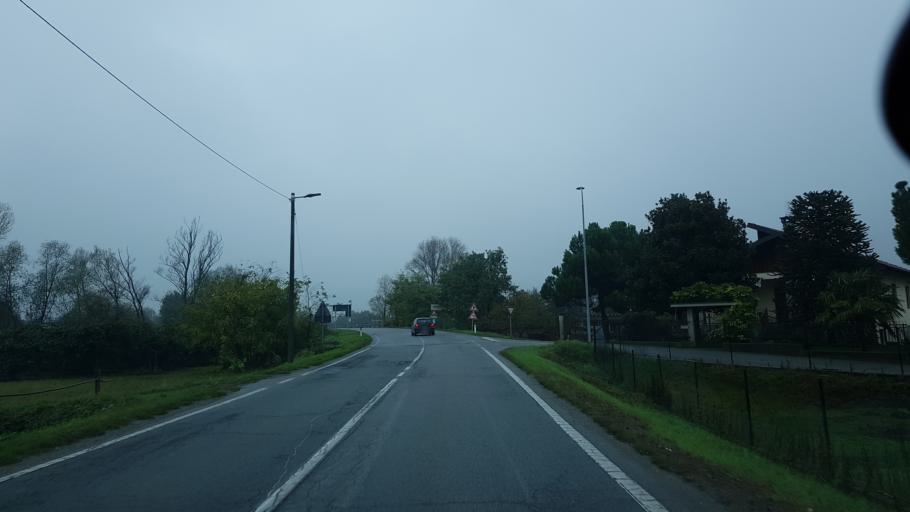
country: IT
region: Piedmont
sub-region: Provincia di Cuneo
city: Vottignasco
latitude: 44.5583
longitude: 7.6197
